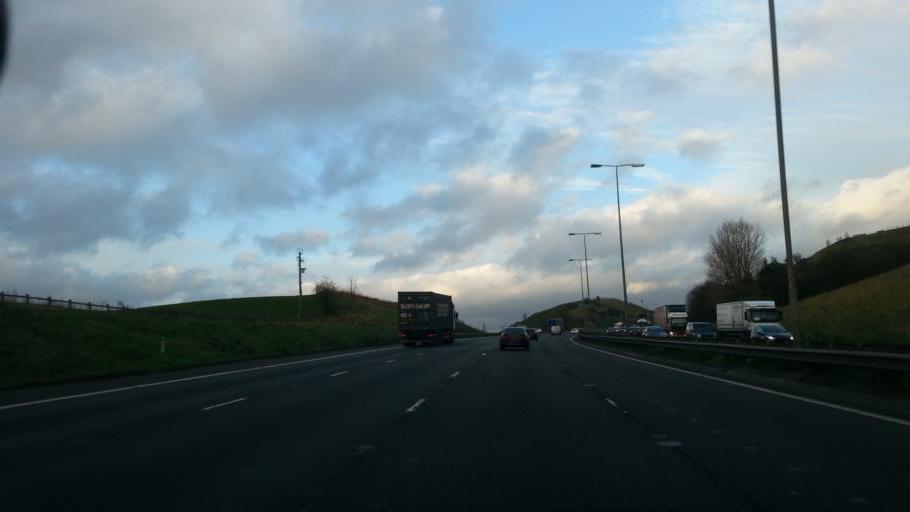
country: GB
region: England
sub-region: Borough of Rochdale
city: Milnrow
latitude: 53.6156
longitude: -2.0885
